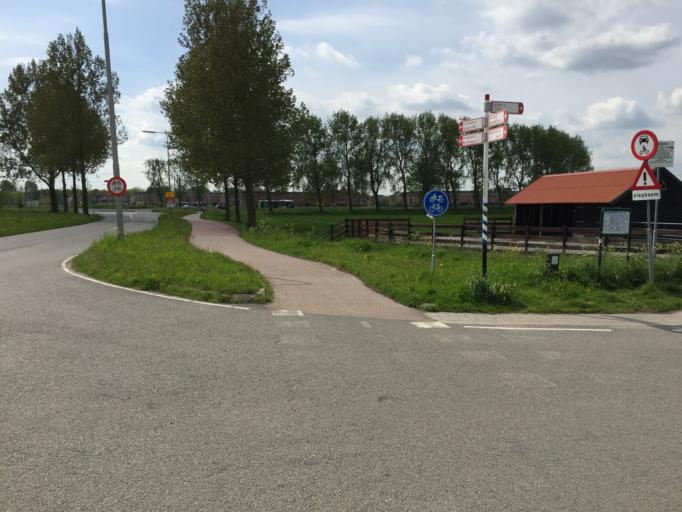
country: NL
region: South Holland
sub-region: Gemeente Leiderdorp
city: Leiderdorp
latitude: 52.1771
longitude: 4.5387
